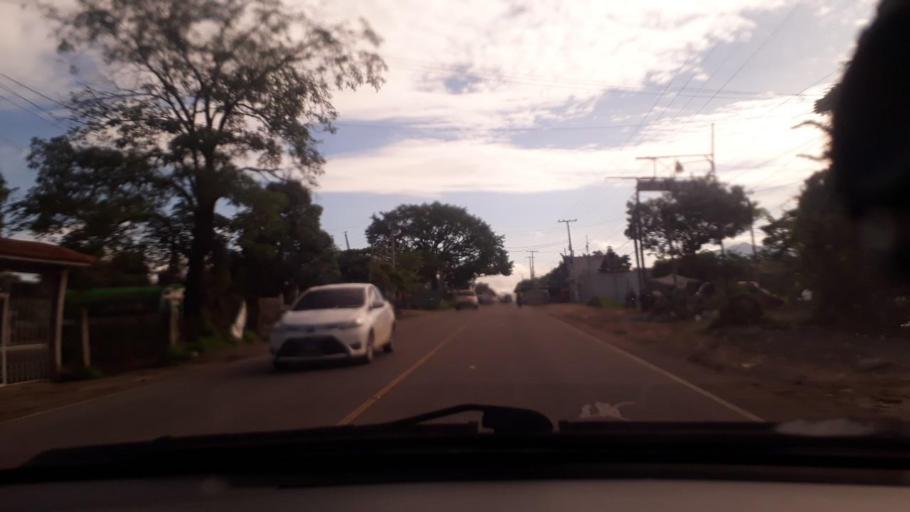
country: GT
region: Jutiapa
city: Jutiapa
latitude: 14.3038
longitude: -89.8714
